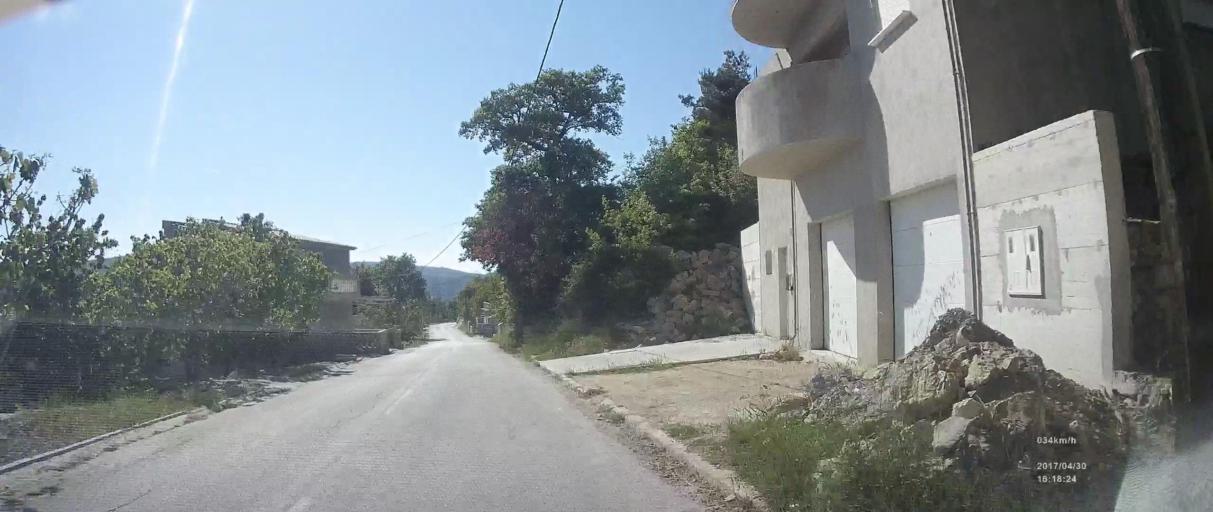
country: HR
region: Splitsko-Dalmatinska
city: Srinjine
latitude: 43.4998
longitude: 16.6080
